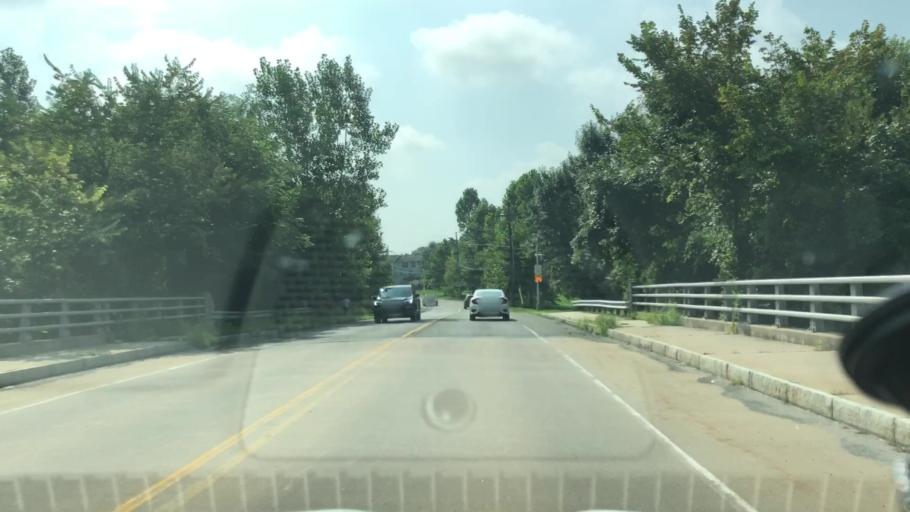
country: US
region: New Jersey
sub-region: Mercer County
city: Lawrenceville
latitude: 40.3024
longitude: -74.6884
